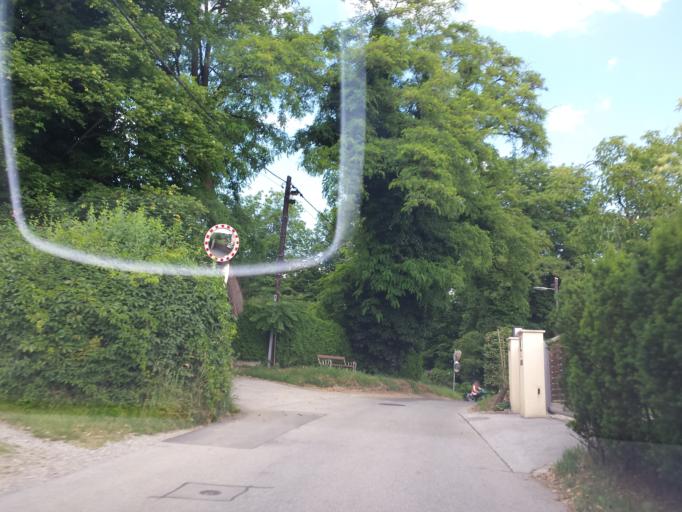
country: AT
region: Styria
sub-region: Graz Stadt
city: Graz
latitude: 47.0928
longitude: 15.4495
